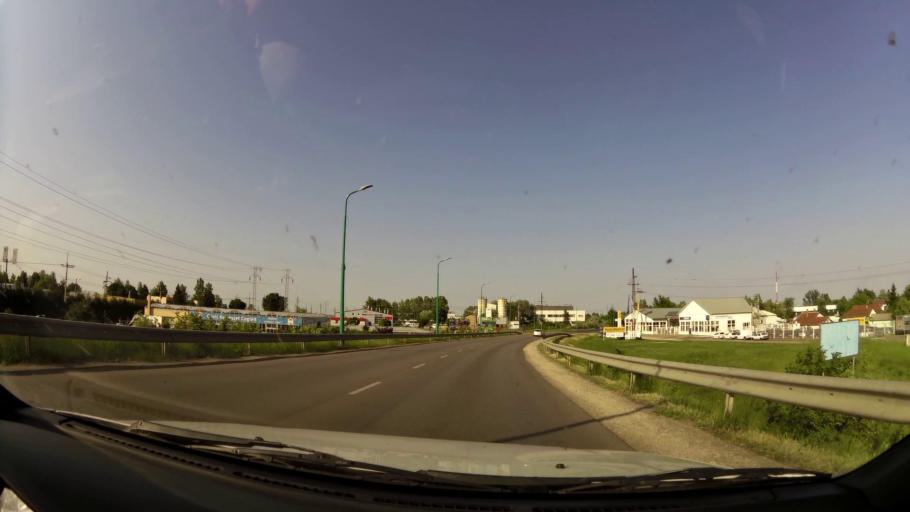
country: HU
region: Pest
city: Cegled
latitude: 47.1869
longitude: 19.7999
